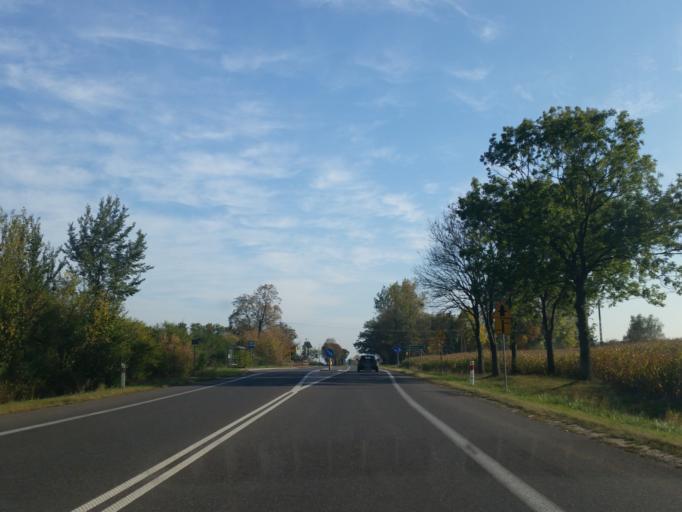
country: PL
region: Masovian Voivodeship
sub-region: Powiat plocki
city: Drobin
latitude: 52.6924
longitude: 20.0486
